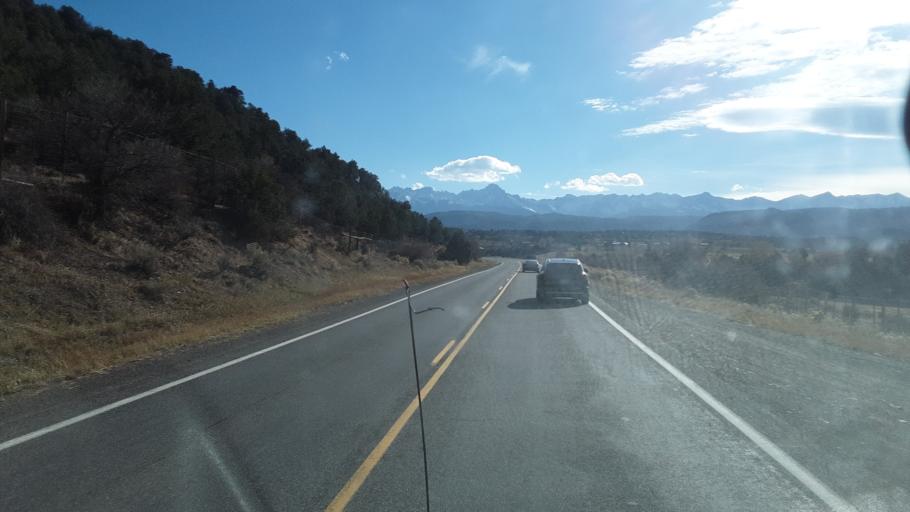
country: US
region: Colorado
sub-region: Ouray County
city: Ouray
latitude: 38.1890
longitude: -107.7456
